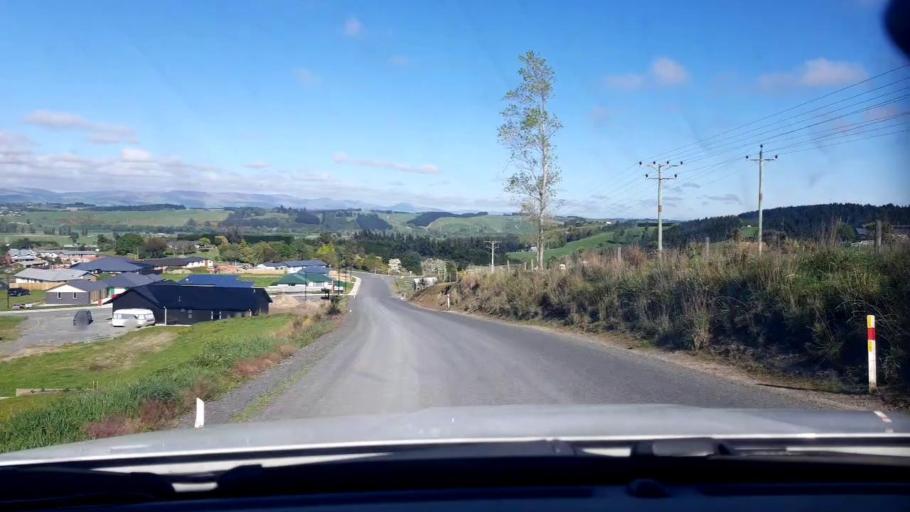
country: NZ
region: Otago
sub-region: Clutha District
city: Balclutha
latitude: -46.2237
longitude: 169.7503
